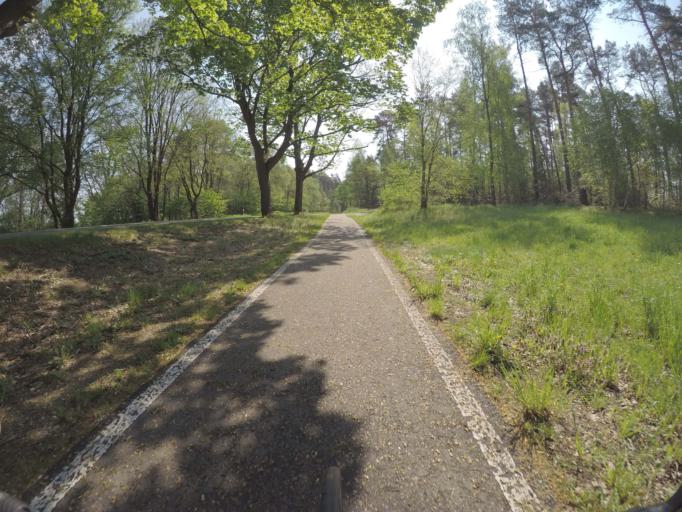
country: DE
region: Brandenburg
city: Wandlitz
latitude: 52.7964
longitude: 13.5164
